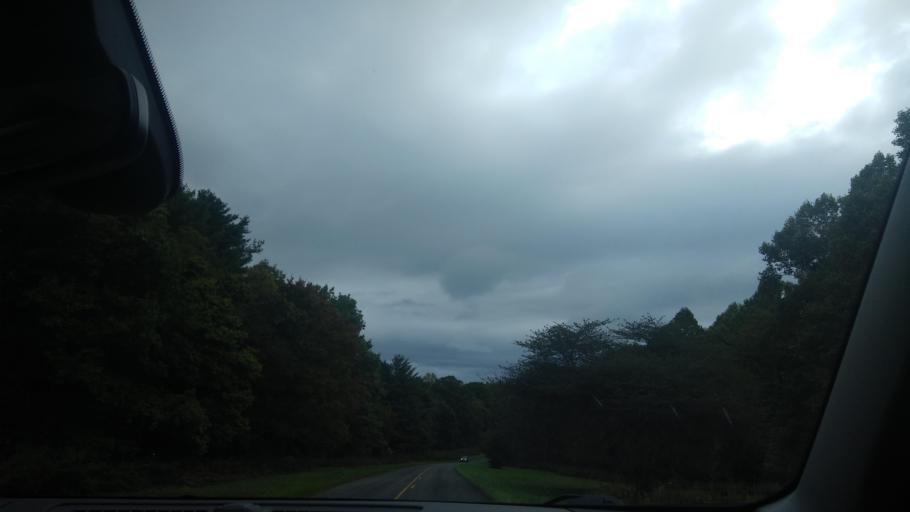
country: US
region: North Carolina
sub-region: Surry County
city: Flat Rock
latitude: 36.6429
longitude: -80.5466
